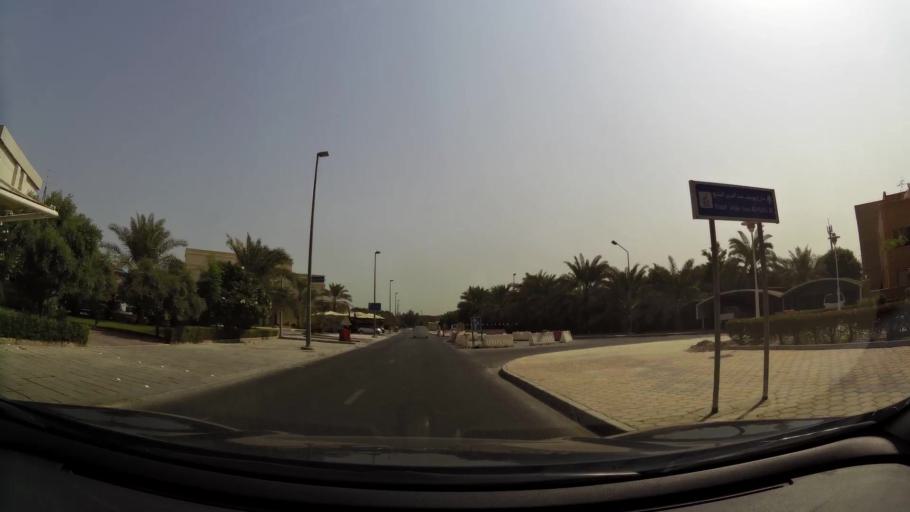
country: KW
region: Al Asimah
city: Ash Shamiyah
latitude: 29.3466
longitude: 47.9577
